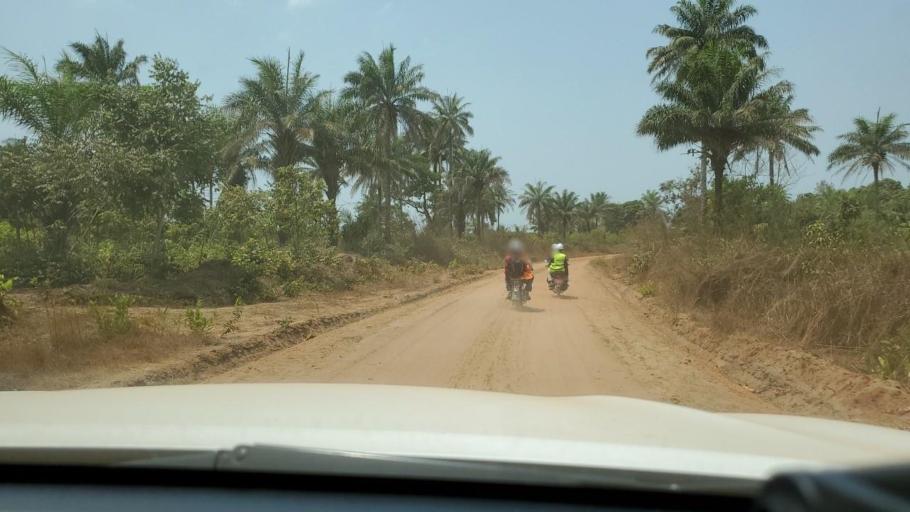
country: GN
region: Boke
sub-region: Boffa
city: Boffa
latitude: 10.0451
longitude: -13.8733
